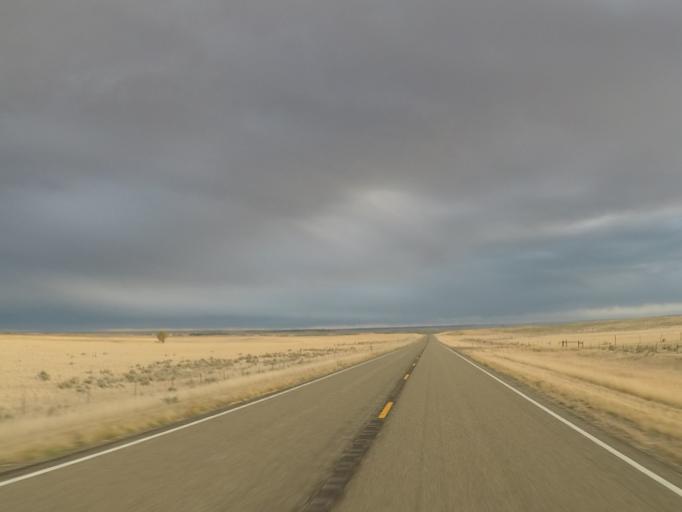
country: US
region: Montana
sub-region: Golden Valley County
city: Ryegate
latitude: 46.3962
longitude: -109.2574
